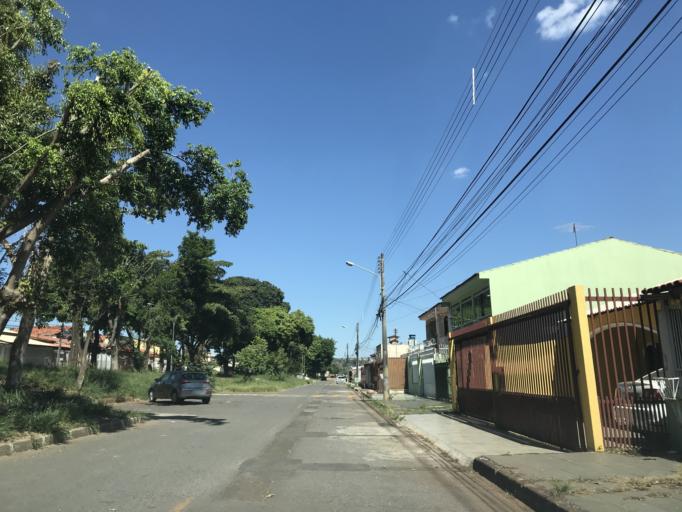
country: BR
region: Federal District
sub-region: Brasilia
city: Brasilia
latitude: -15.6567
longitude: -47.8078
